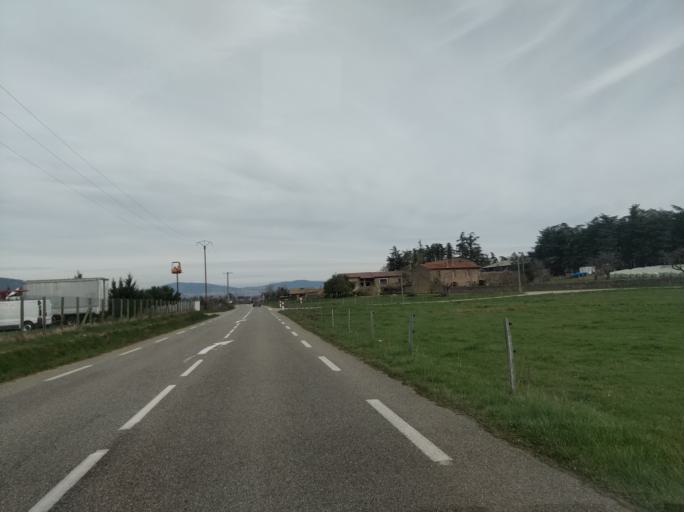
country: FR
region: Rhone-Alpes
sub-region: Departement de l'Ardeche
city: Roiffieux
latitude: 45.2109
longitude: 4.6597
